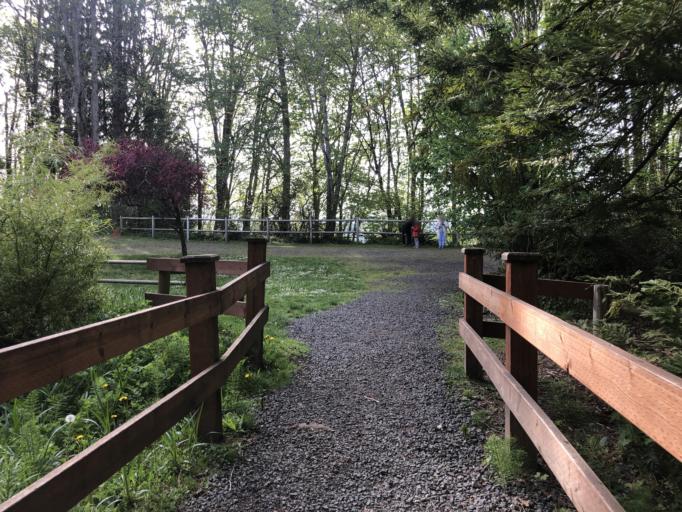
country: US
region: Washington
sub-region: Kitsap County
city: Silverdale
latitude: 47.6331
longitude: -122.6722
